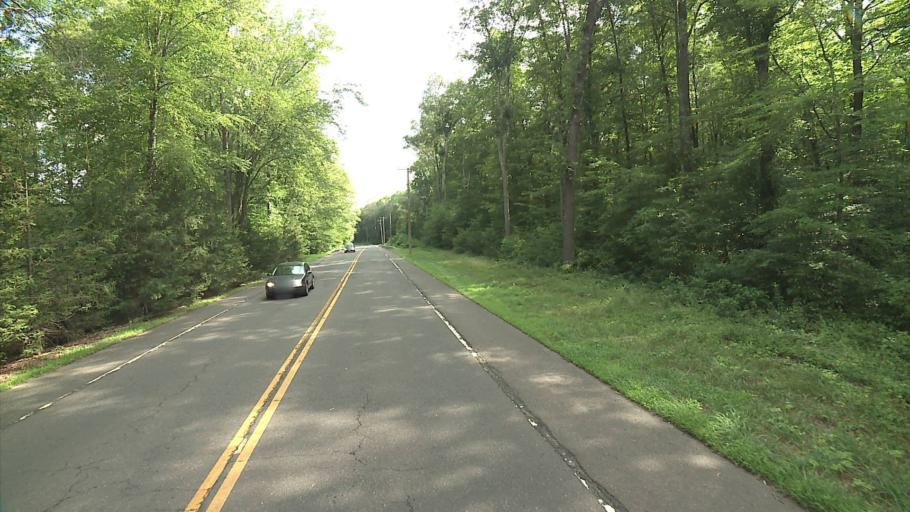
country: US
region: Connecticut
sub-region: Middlesex County
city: Clinton
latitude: 41.3261
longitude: -72.4924
